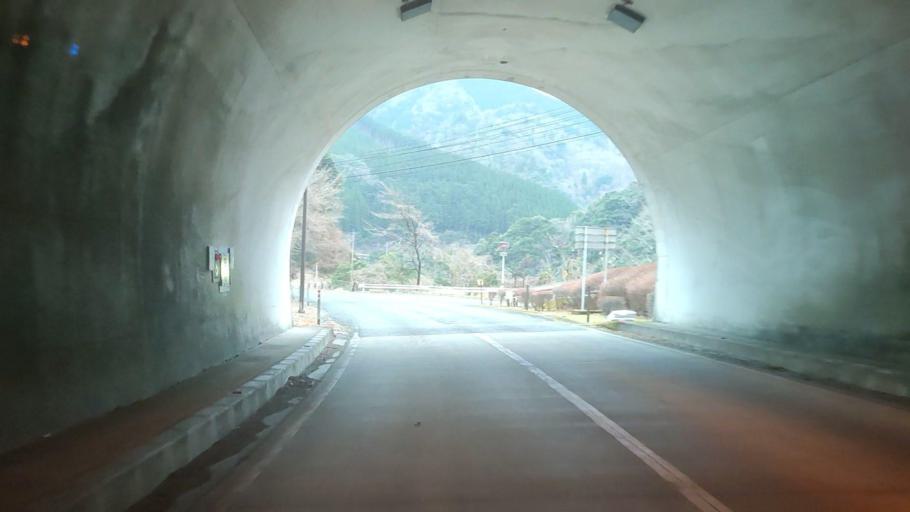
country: JP
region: Kumamoto
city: Matsubase
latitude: 32.5036
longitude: 130.9157
